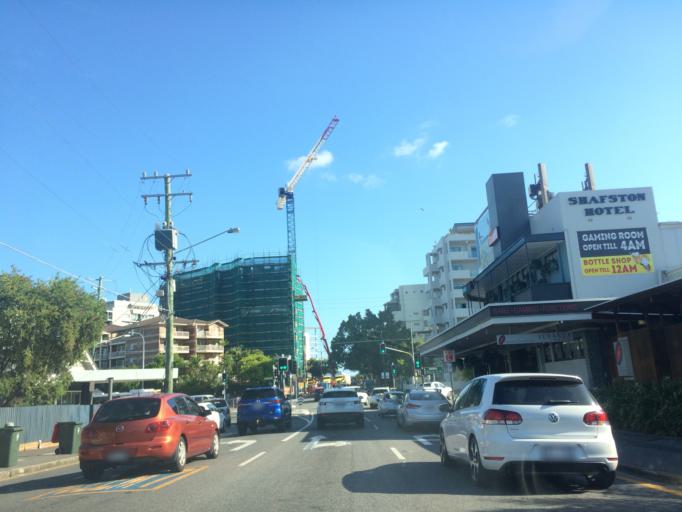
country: AU
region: Queensland
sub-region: Brisbane
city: Woolloongabba
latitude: -27.4795
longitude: 153.0414
